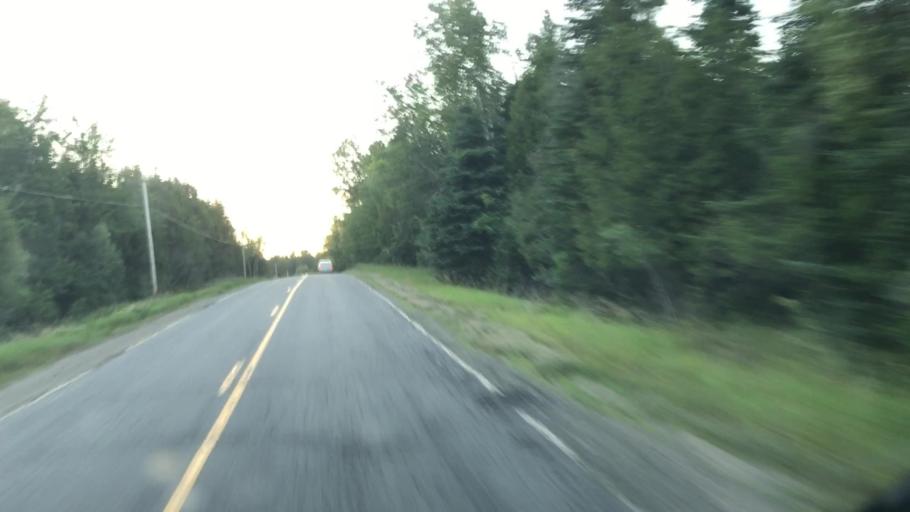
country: US
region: Maine
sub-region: Penobscot County
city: Medway
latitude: 45.6038
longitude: -68.2525
